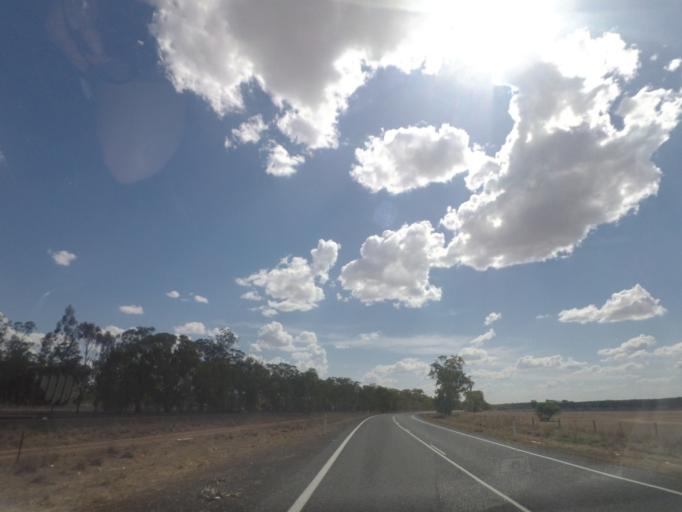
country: AU
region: Queensland
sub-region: Southern Downs
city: Stanthorpe
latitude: -28.3938
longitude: 151.3146
